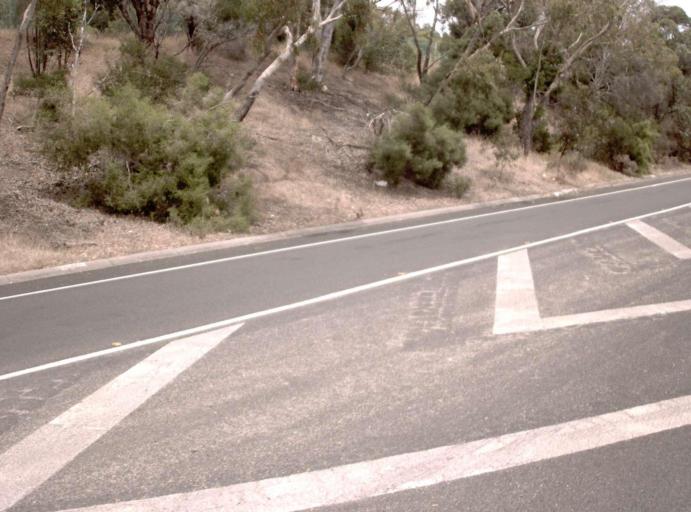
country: AU
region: Victoria
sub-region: Mornington Peninsula
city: McCrae
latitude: -38.3535
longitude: 144.9311
